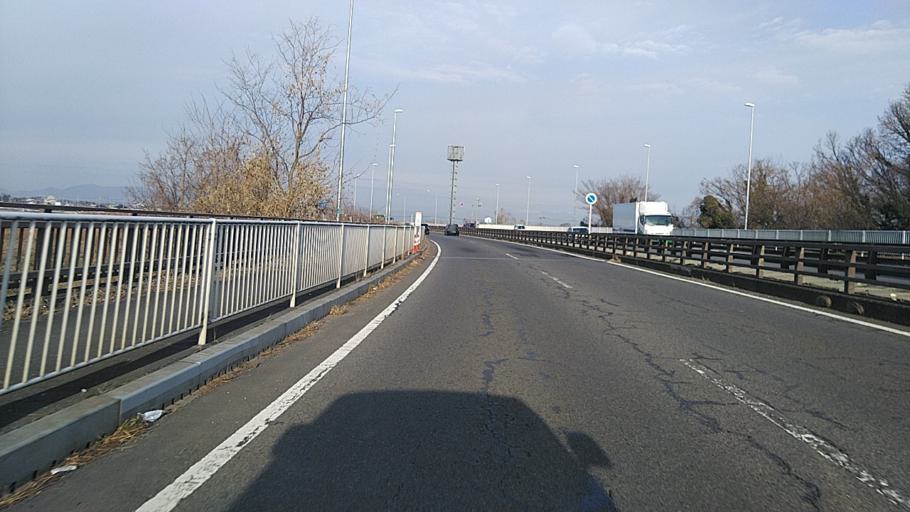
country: JP
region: Tochigi
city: Oyama
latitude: 36.3086
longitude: 139.7854
